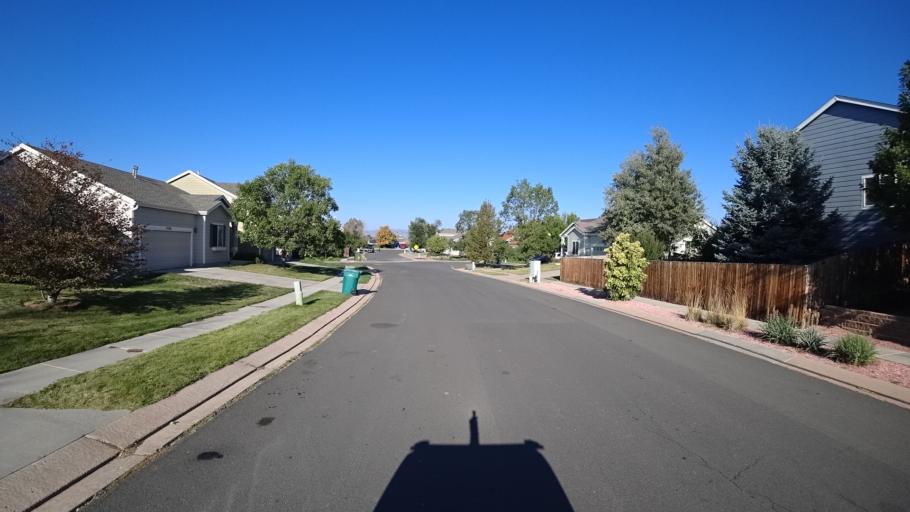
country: US
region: Colorado
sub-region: El Paso County
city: Cimarron Hills
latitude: 38.8858
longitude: -104.6931
